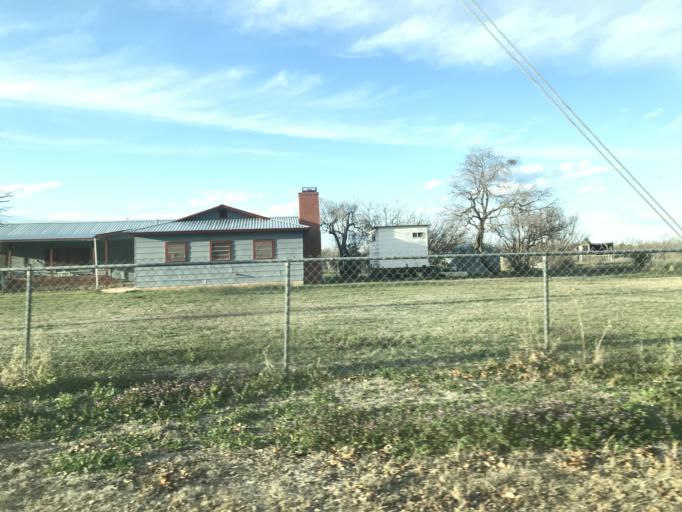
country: US
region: Texas
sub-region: Tom Green County
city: San Angelo
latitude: 31.4973
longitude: -100.4424
